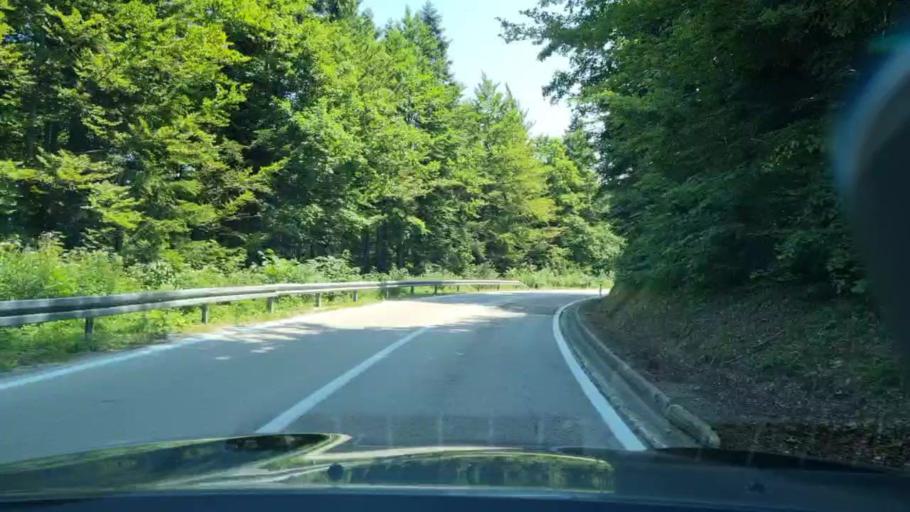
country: BA
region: Federation of Bosnia and Herzegovina
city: Sanica
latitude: 44.4885
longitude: 16.4000
